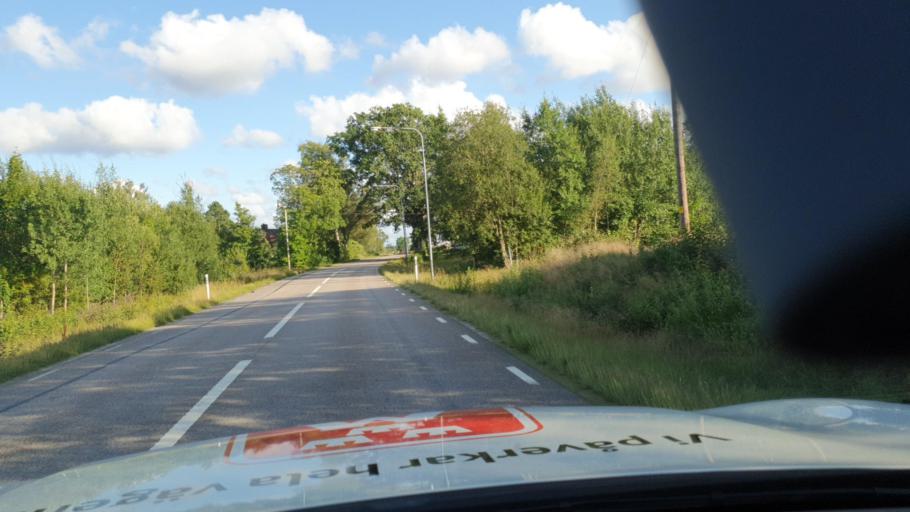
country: SE
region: Vaestra Goetaland
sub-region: Vanersborgs Kommun
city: Vanersborg
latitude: 58.4900
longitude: 12.2559
